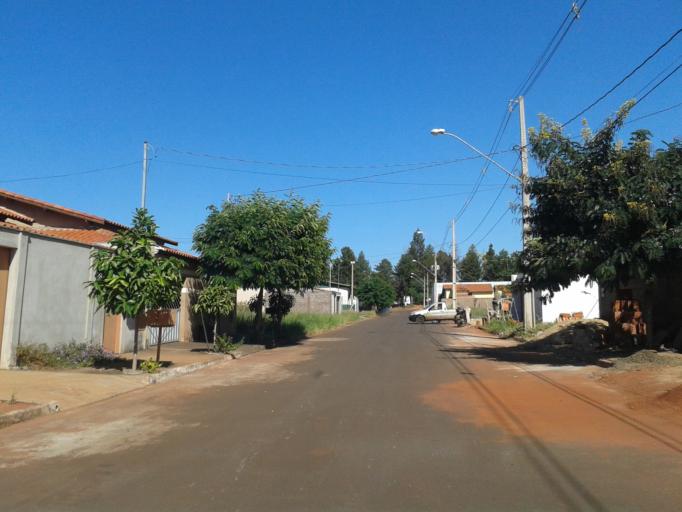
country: BR
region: Minas Gerais
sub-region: Santa Vitoria
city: Santa Vitoria
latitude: -18.8561
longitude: -50.1276
